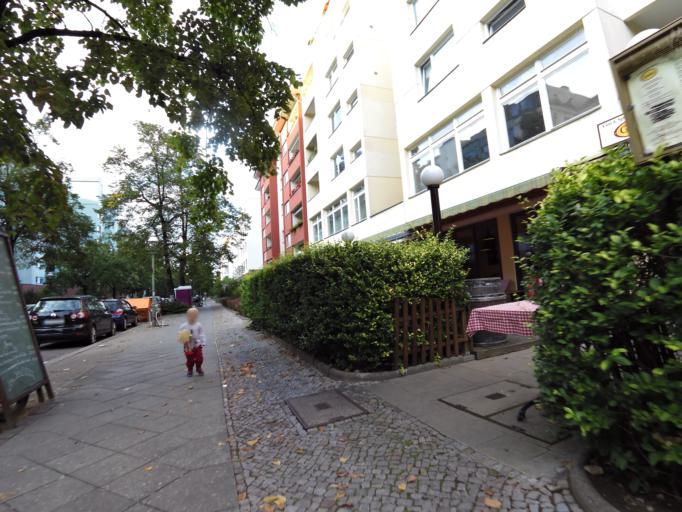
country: DE
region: Berlin
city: Wilmersdorf Bezirk
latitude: 52.4887
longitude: 13.3288
